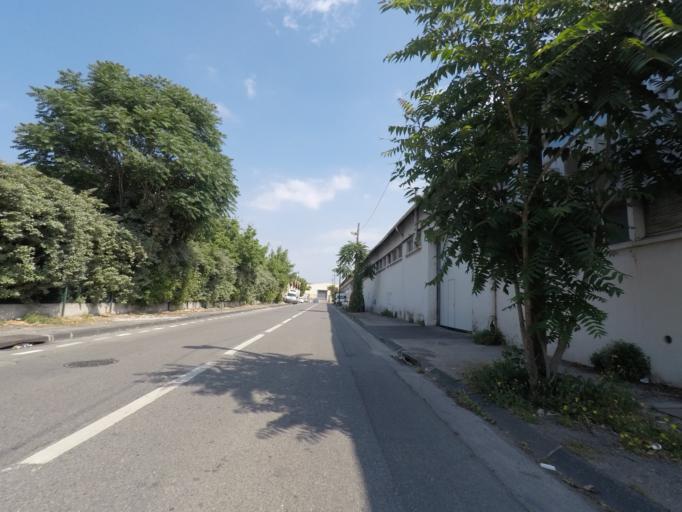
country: FR
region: Provence-Alpes-Cote d'Azur
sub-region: Departement des Bouches-du-Rhone
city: Marseille 10
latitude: 43.2769
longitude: 5.4036
